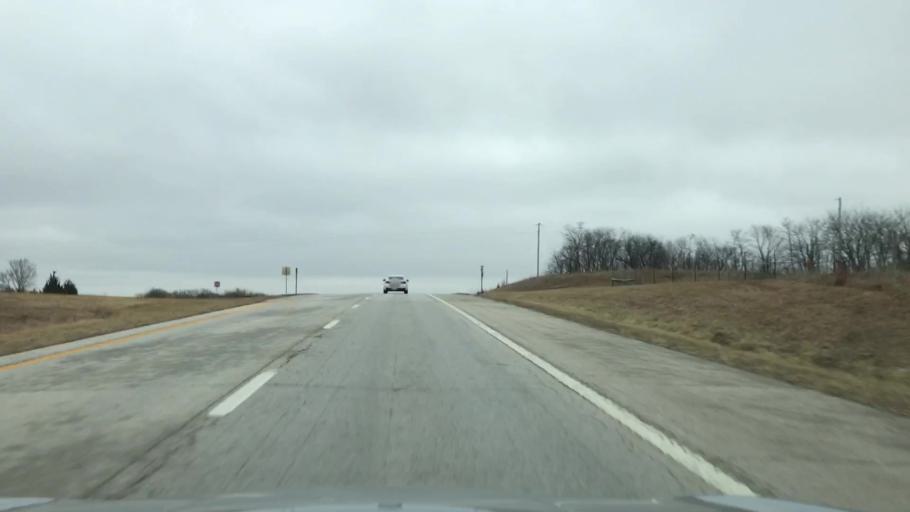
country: US
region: Missouri
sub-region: Linn County
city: Marceline
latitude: 39.7590
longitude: -92.8719
